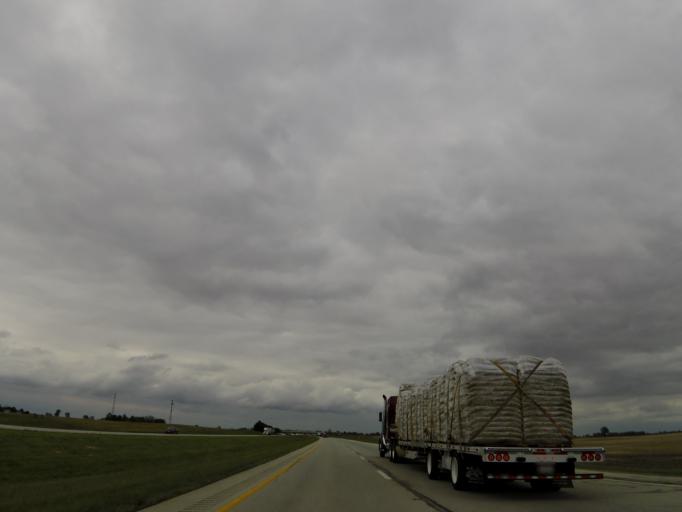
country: US
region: Ohio
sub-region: Greene County
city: Jamestown
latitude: 39.5596
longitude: -83.7145
